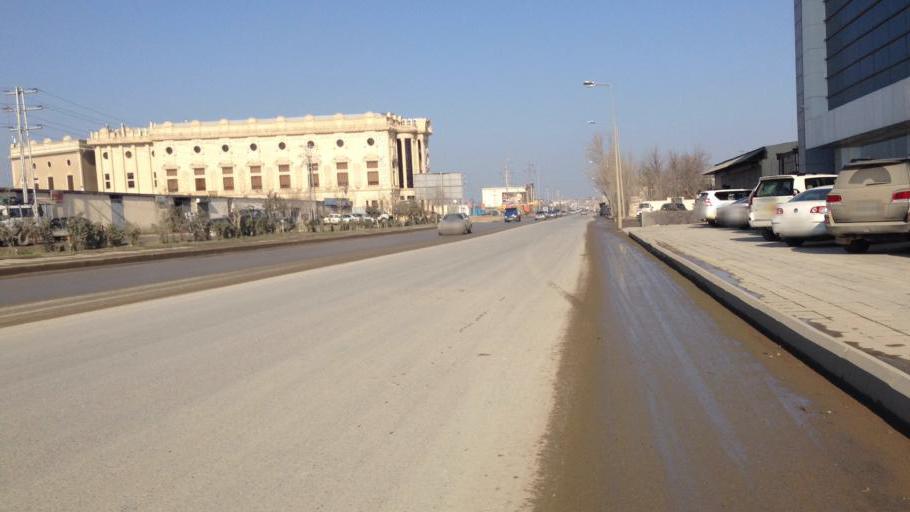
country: AZ
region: Baki
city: Binagadi
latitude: 40.4444
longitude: 49.8444
